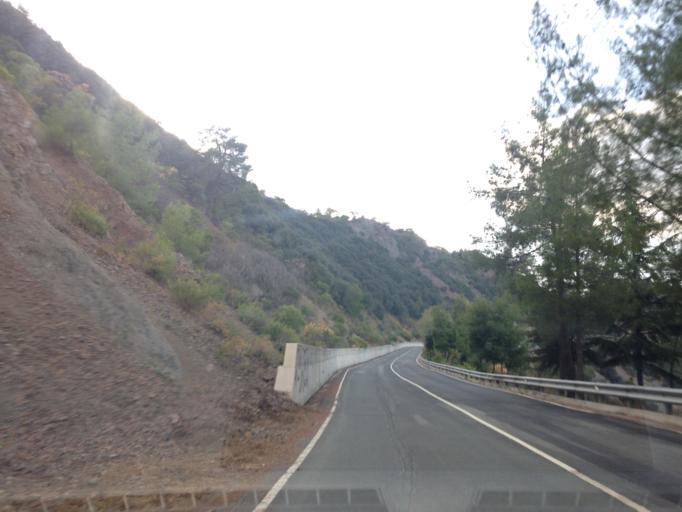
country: CY
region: Lefkosia
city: Kakopetria
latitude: 34.9865
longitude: 32.7435
